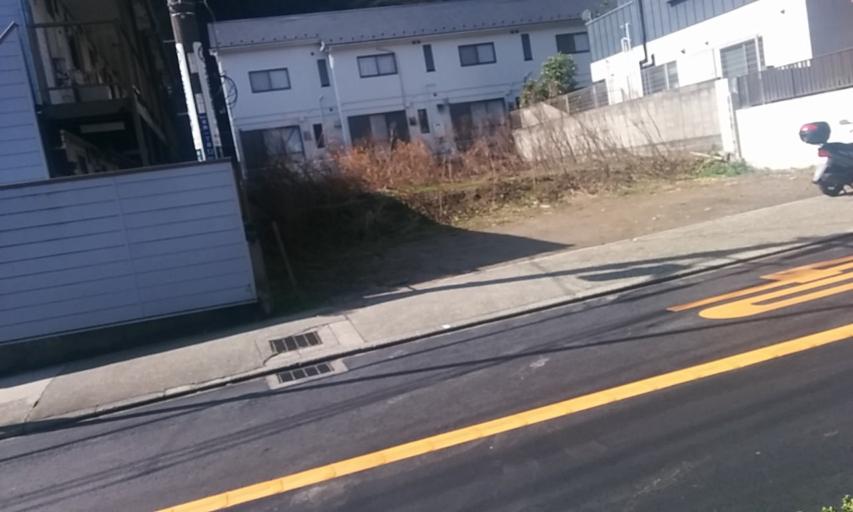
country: JP
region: Kanagawa
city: Kamakura
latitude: 35.3207
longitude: 139.5422
